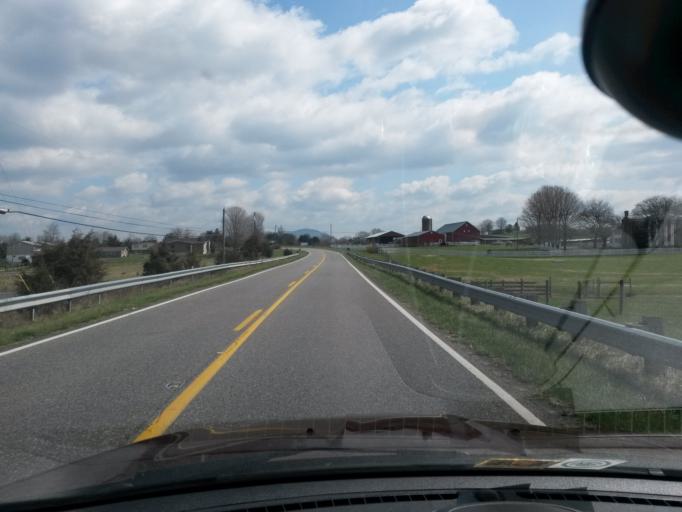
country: US
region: Virginia
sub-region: Augusta County
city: Weyers Cave
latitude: 38.3280
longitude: -78.8693
